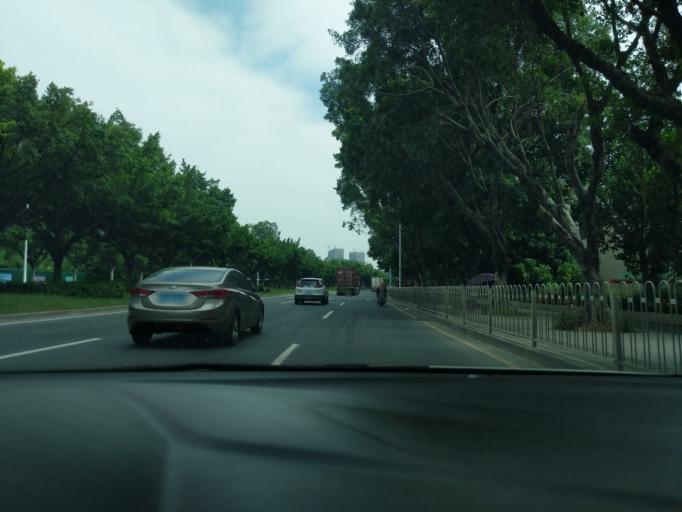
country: CN
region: Guangdong
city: Nansha
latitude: 22.7540
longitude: 113.5751
